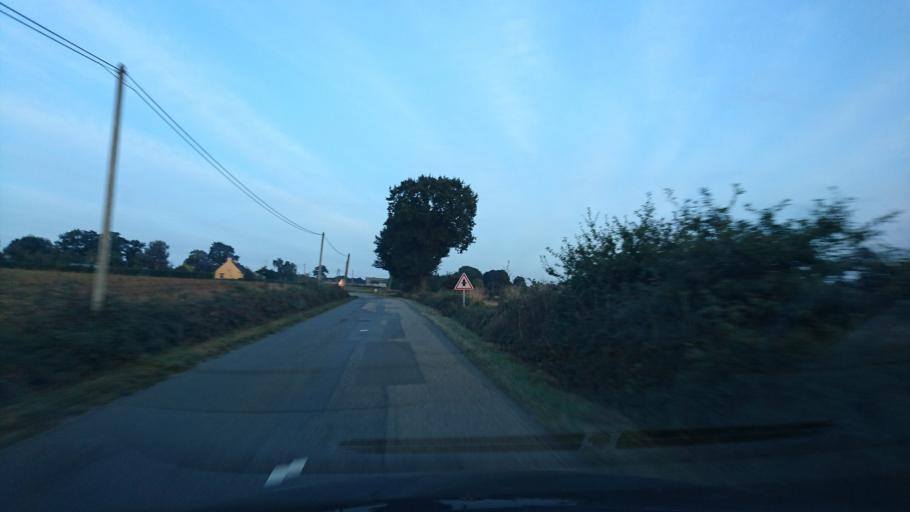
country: FR
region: Brittany
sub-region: Departement d'Ille-et-Vilaine
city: Maure-de-Bretagne
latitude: 47.9005
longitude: -1.9446
